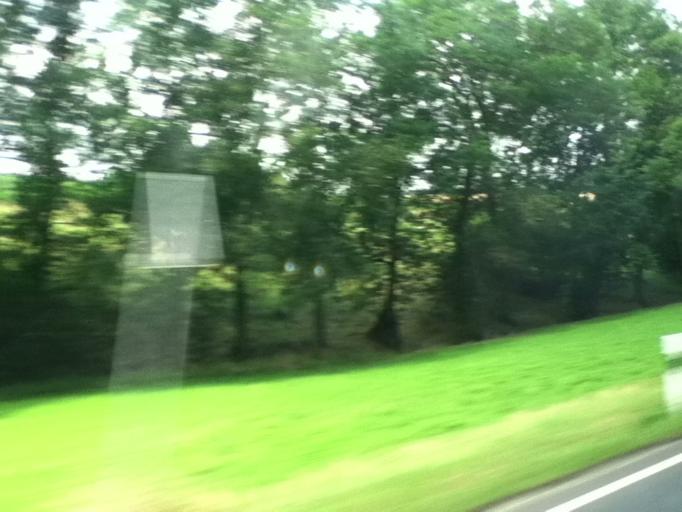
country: DE
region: Thuringia
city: Kapellendorf
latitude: 50.9618
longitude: 11.4683
